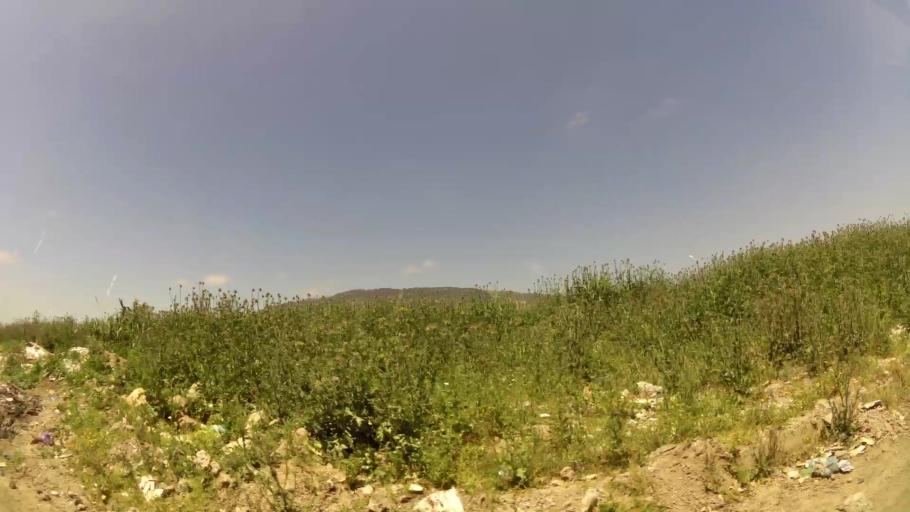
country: MA
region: Fes-Boulemane
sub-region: Fes
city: Fes
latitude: 34.0434
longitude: -5.0460
